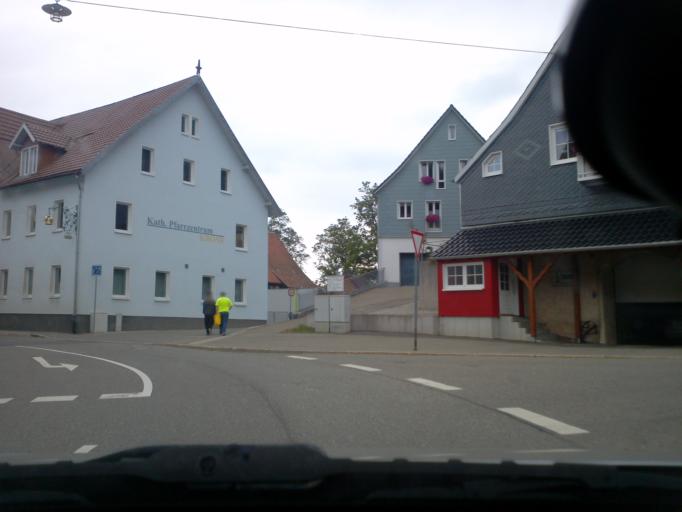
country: DE
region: Baden-Wuerttemberg
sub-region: Freiburg Region
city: Vohrenbach
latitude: 48.0449
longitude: 8.3060
